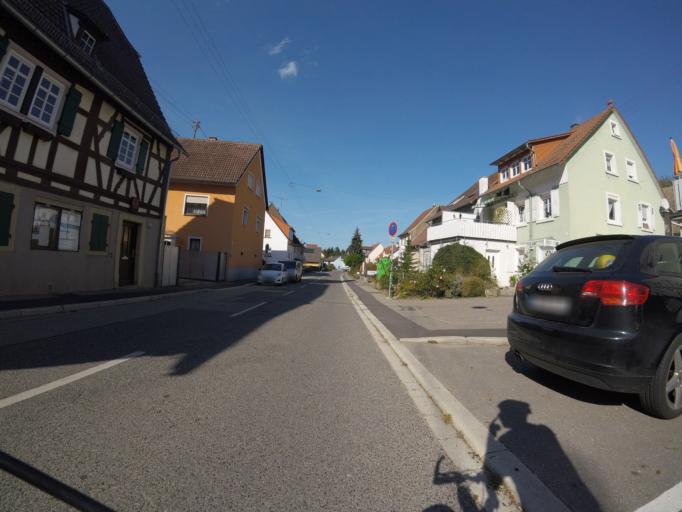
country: DE
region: Baden-Wuerttemberg
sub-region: Karlsruhe Region
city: Bretten
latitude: 49.0068
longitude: 8.7248
